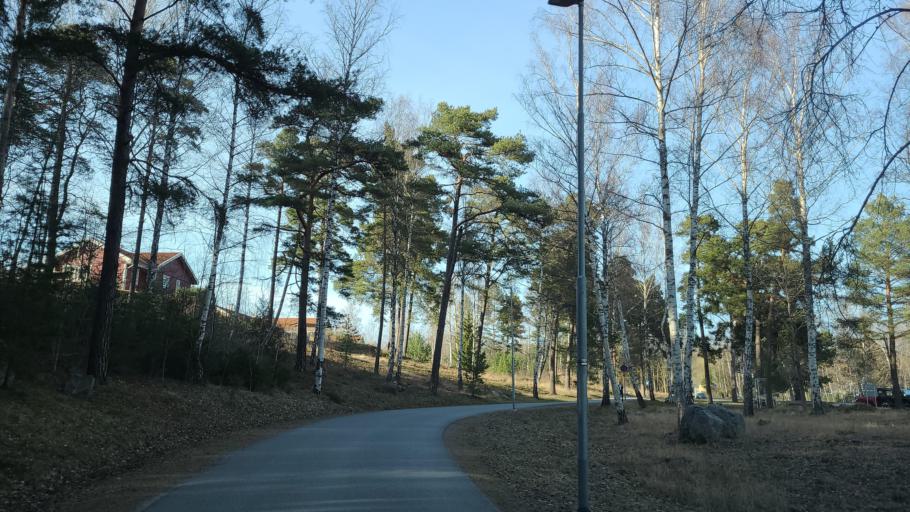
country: SE
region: Stockholm
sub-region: Ekero Kommun
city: Ekeroe
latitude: 59.2677
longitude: 17.7802
